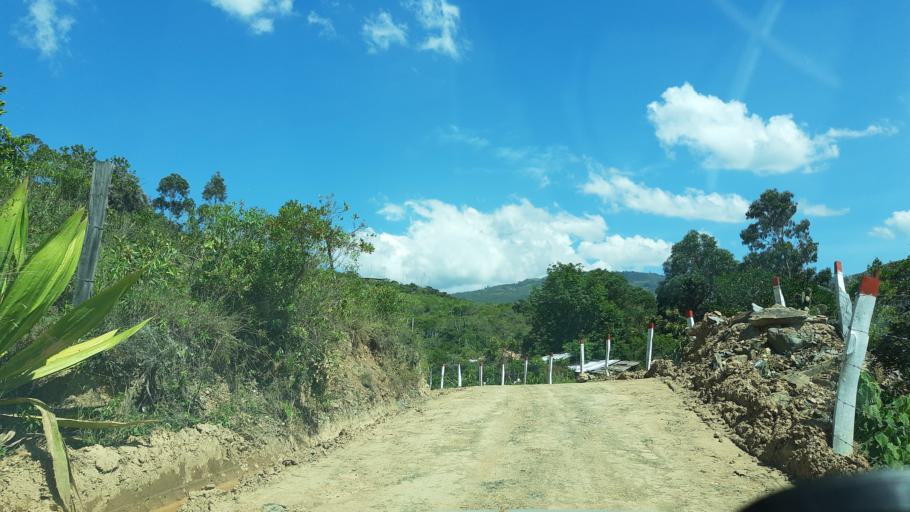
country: CO
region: Boyaca
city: Santa Sofia
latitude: 5.6953
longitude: -73.5774
